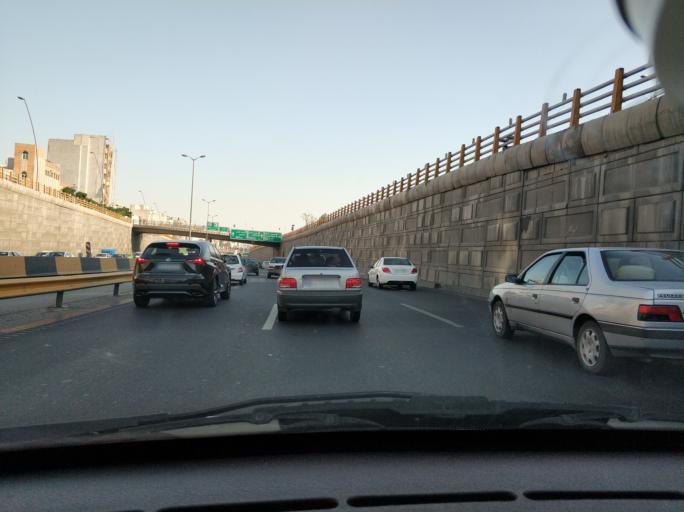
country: IR
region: Tehran
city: Tehran
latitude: 35.6951
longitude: 51.4565
